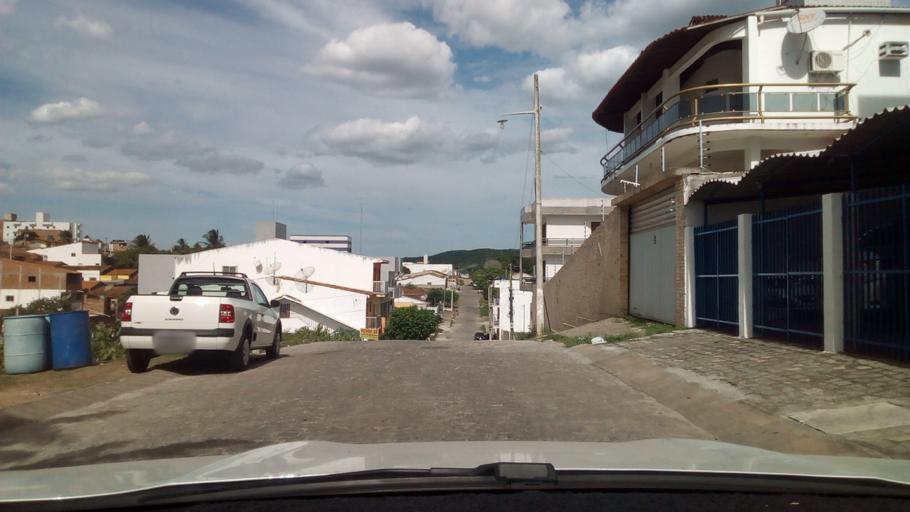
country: BR
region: Paraiba
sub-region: Guarabira
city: Guarabira
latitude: -6.8447
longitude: -35.4969
